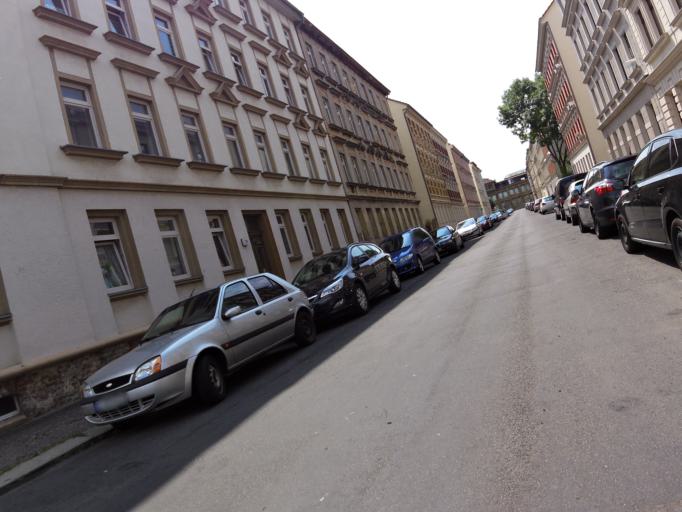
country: DE
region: Saxony
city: Taucha
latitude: 51.3476
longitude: 12.4510
